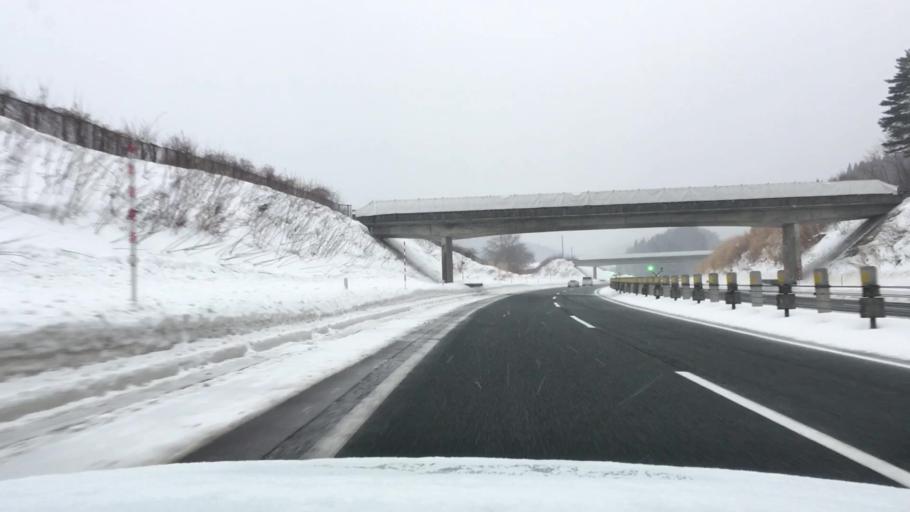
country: JP
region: Akita
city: Hanawa
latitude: 40.1093
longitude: 141.0409
